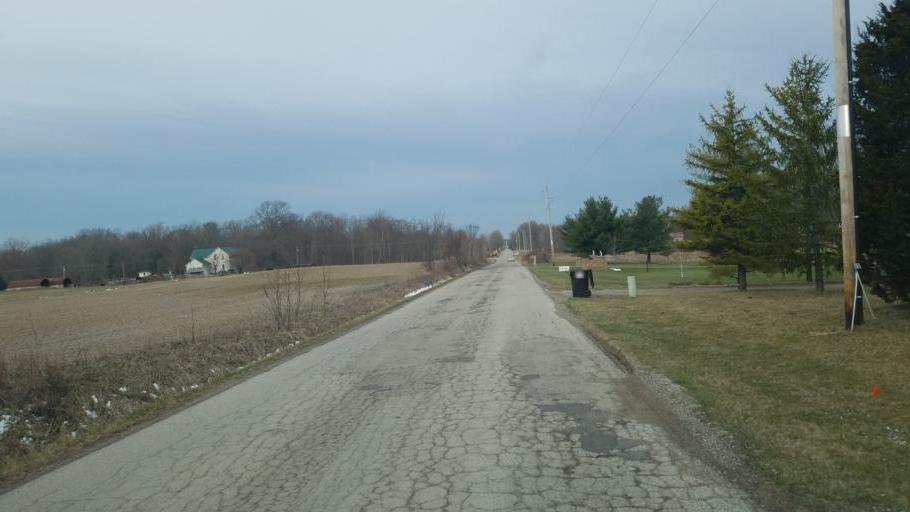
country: US
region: Ohio
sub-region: Morrow County
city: Mount Gilead
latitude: 40.4951
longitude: -82.8165
